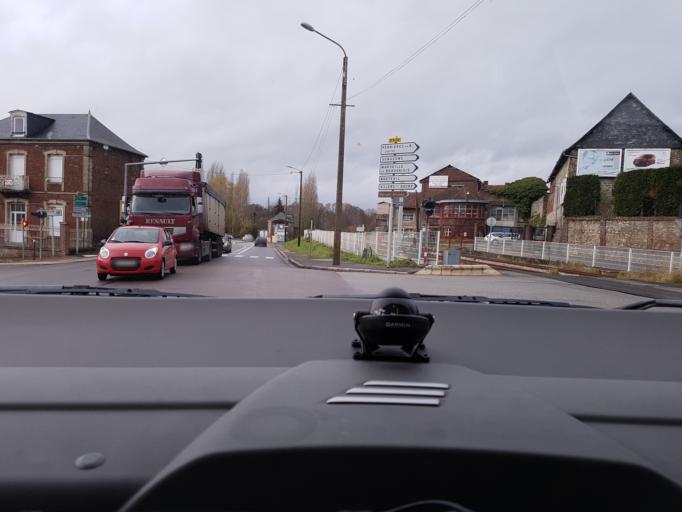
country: FR
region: Haute-Normandie
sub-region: Departement de la Seine-Maritime
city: Gournay-en-Bray
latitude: 49.4833
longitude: 1.7350
